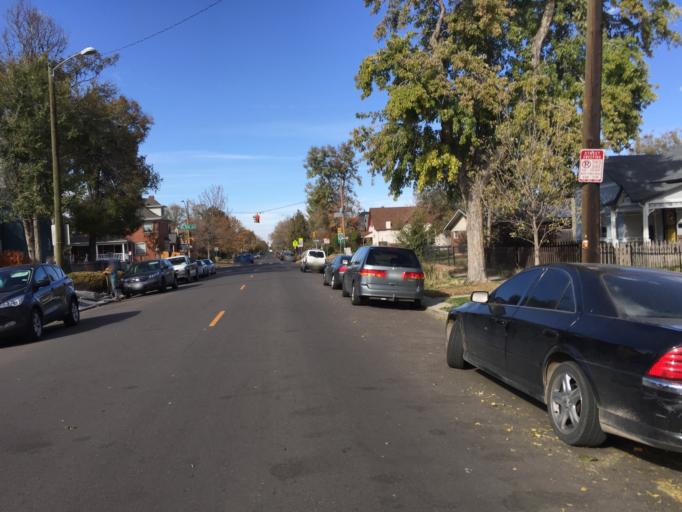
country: US
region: Colorado
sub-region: Denver County
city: Denver
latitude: 39.7601
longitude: -104.9684
